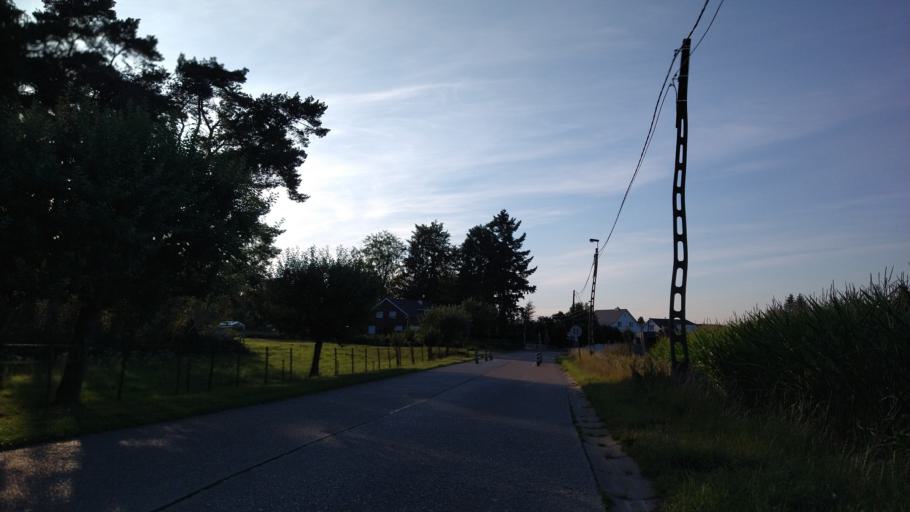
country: BE
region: Flanders
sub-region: Provincie Vlaams-Brabant
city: Bertem
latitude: 50.8404
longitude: 4.5947
